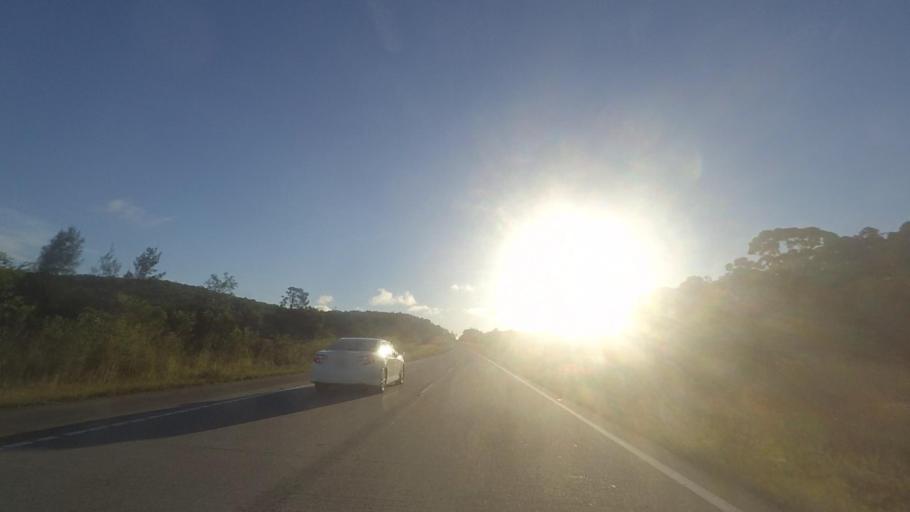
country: AU
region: New South Wales
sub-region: Great Lakes
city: Bulahdelah
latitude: -32.5303
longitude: 152.1862
